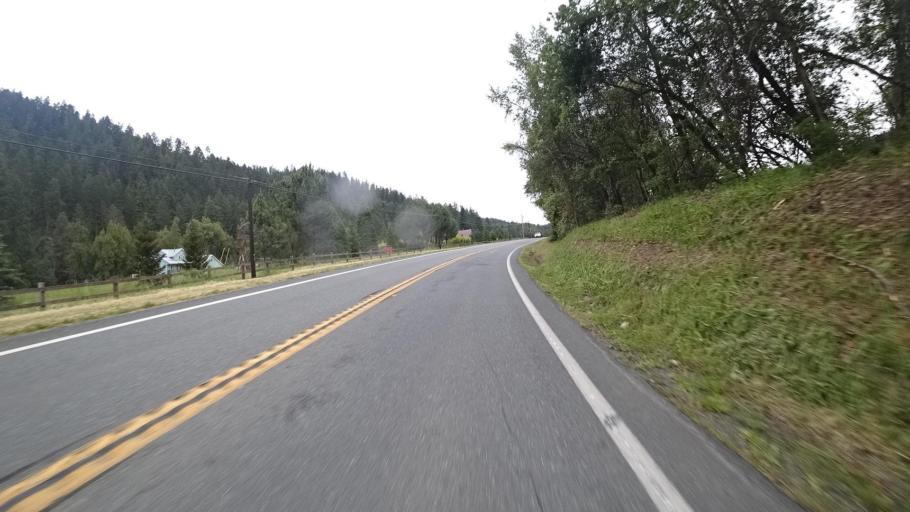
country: US
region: California
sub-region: Humboldt County
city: Willow Creek
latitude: 40.9549
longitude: -123.6432
